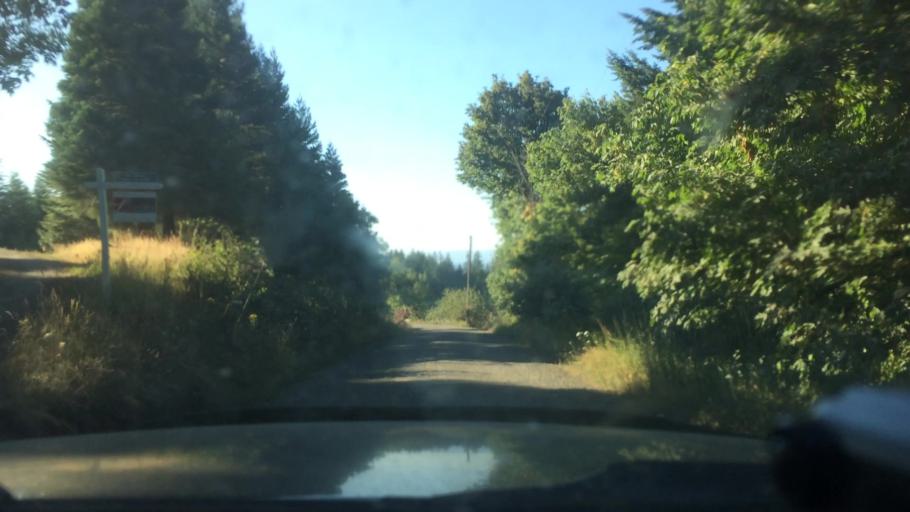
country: US
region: Oregon
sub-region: Yamhill County
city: Newberg
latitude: 45.3618
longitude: -122.9771
